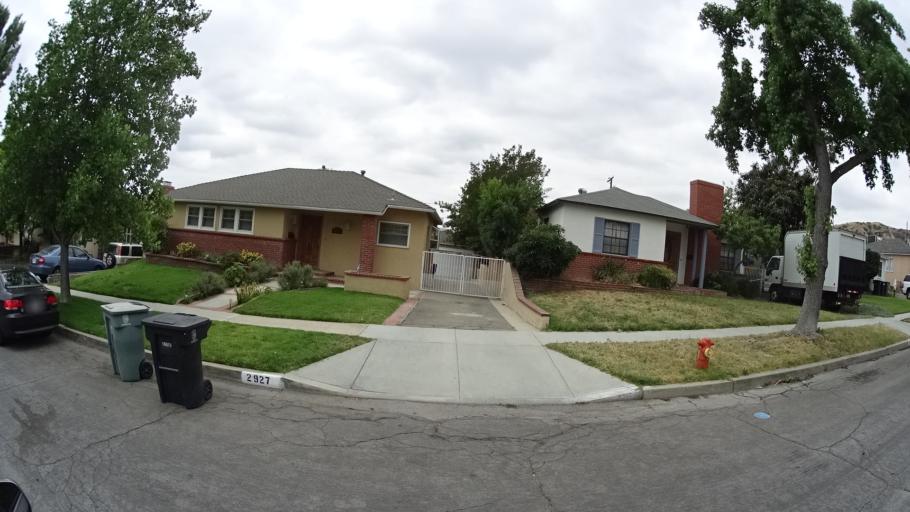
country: US
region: California
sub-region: Los Angeles County
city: Burbank
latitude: 34.2092
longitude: -118.3364
